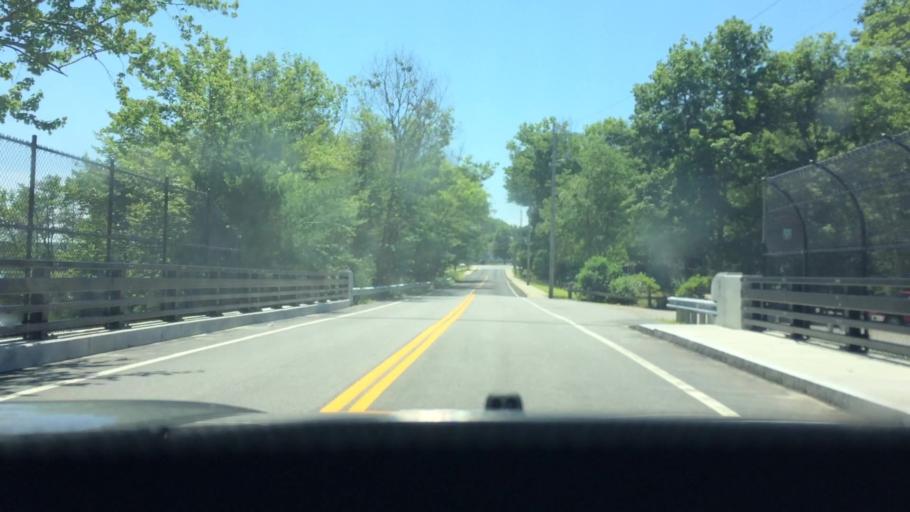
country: US
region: Rhode Island
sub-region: Providence County
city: Harrisville
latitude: 41.9710
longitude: -71.6785
